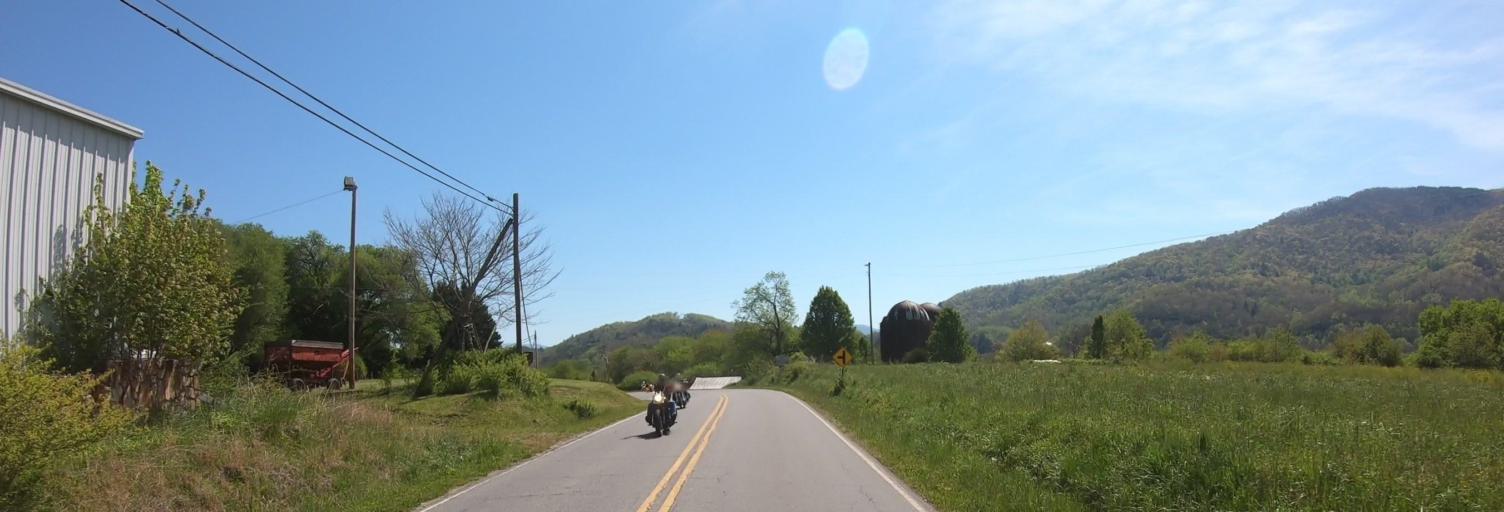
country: US
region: North Carolina
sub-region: Swain County
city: Bryson City
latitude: 35.4366
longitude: -83.4086
